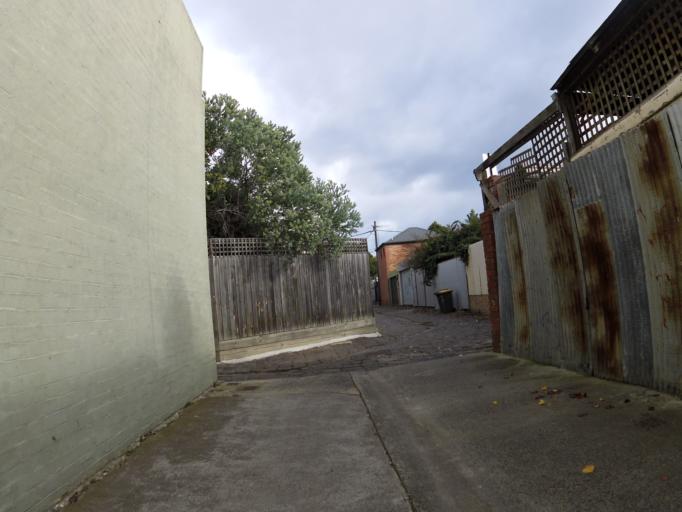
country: AU
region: Victoria
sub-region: Yarra
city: Clifton Hill
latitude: -37.7887
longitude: 144.9991
